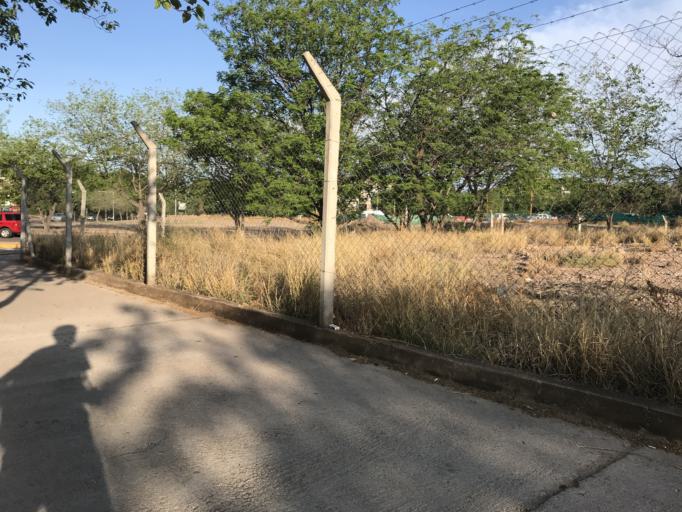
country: AR
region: Mendoza
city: Mendoza
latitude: -32.8787
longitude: -68.8394
